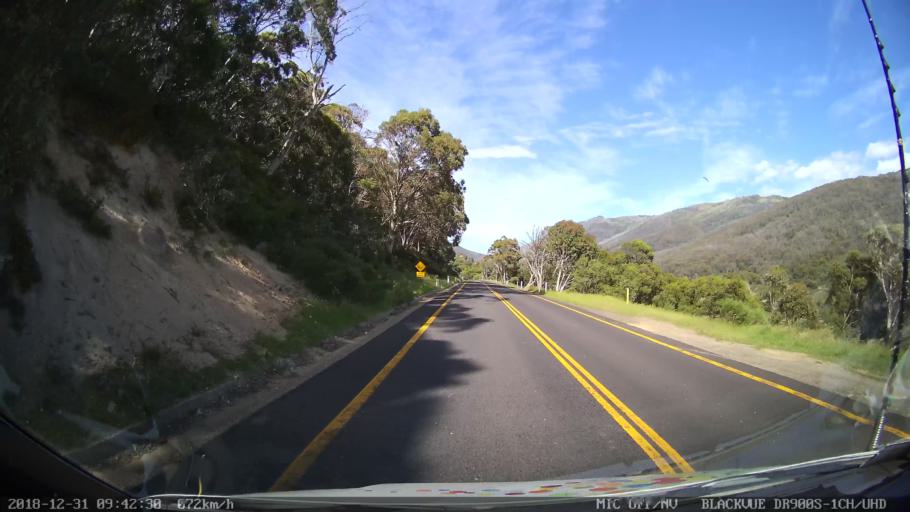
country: AU
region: New South Wales
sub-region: Snowy River
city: Jindabyne
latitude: -36.4968
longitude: 148.3221
